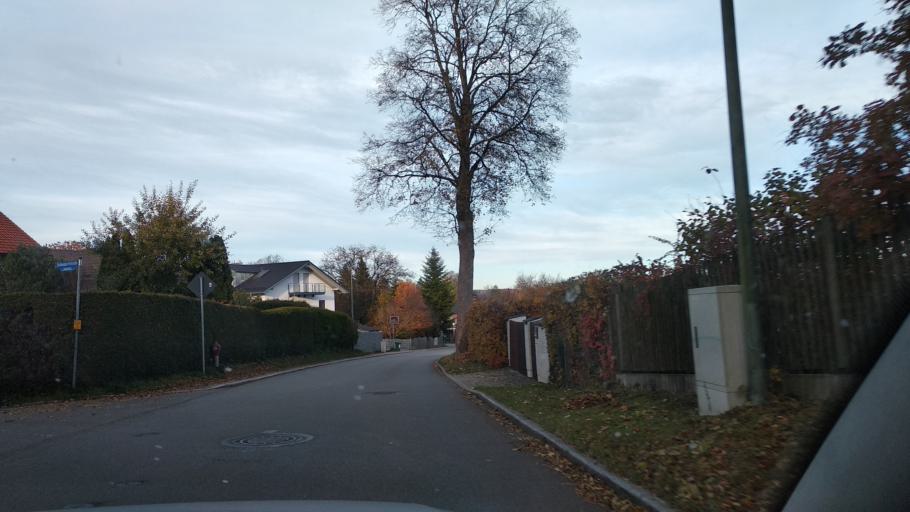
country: DE
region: Bavaria
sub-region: Upper Bavaria
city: Grafing bei Munchen
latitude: 48.0439
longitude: 11.9551
